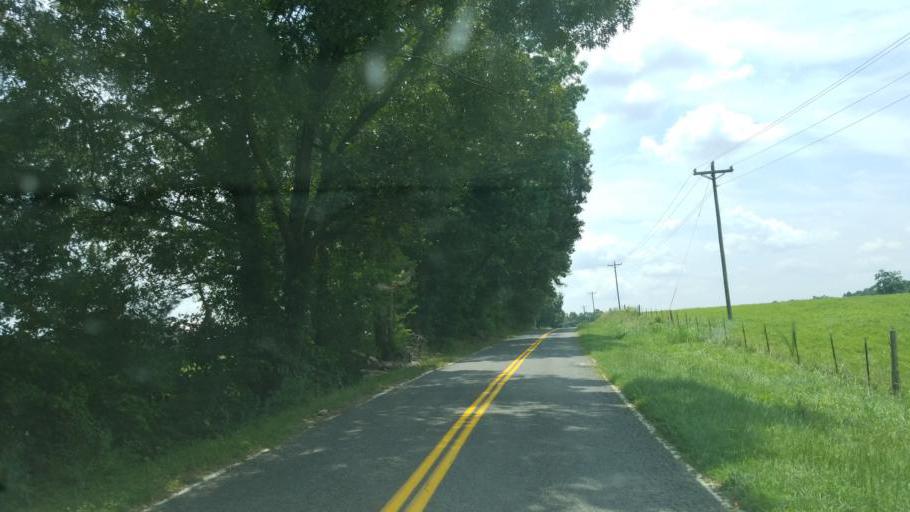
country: US
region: South Carolina
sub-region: Cherokee County
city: Blacksburg
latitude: 35.0835
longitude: -81.4007
